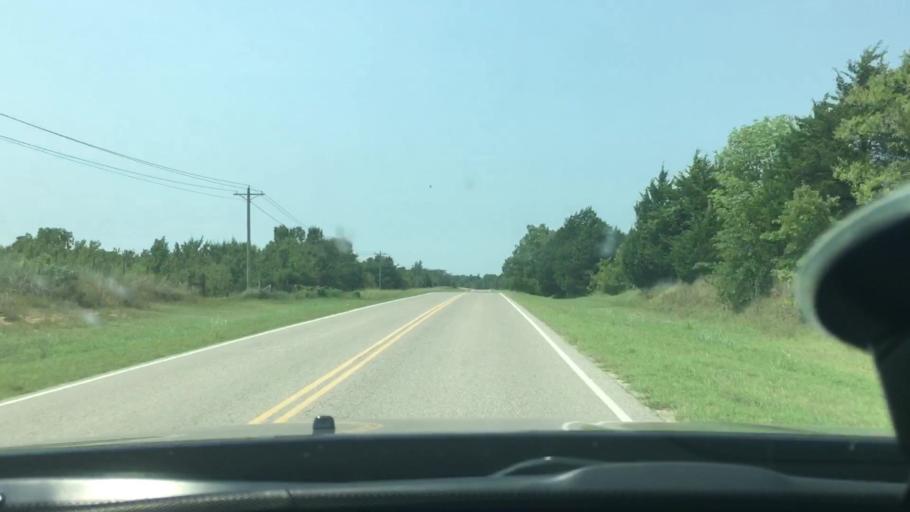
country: US
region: Oklahoma
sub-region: Love County
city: Marietta
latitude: 33.9706
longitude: -97.0112
